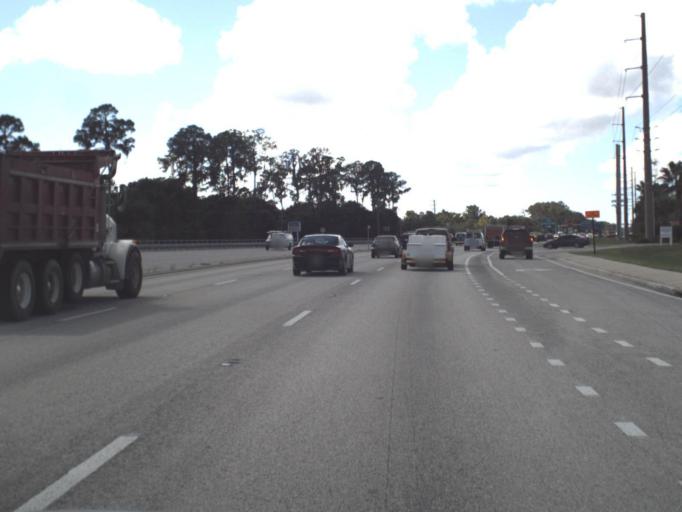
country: US
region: Florida
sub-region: Sarasota County
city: The Meadows
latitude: 27.4323
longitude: -82.4295
